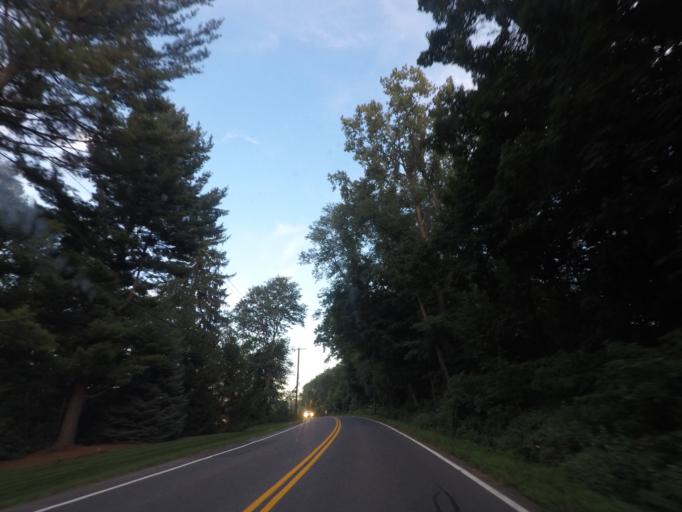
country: US
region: New York
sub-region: Schenectady County
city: Niskayuna
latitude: 42.7728
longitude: -73.8177
